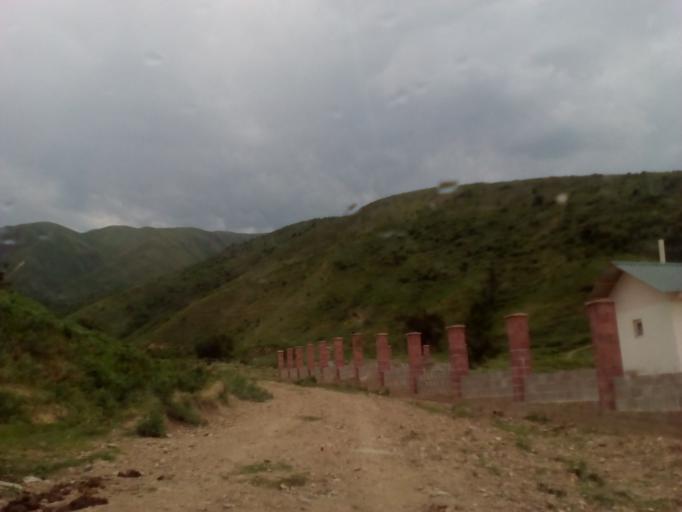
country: KZ
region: Almaty Oblysy
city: Burunday
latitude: 43.1492
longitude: 76.3857
